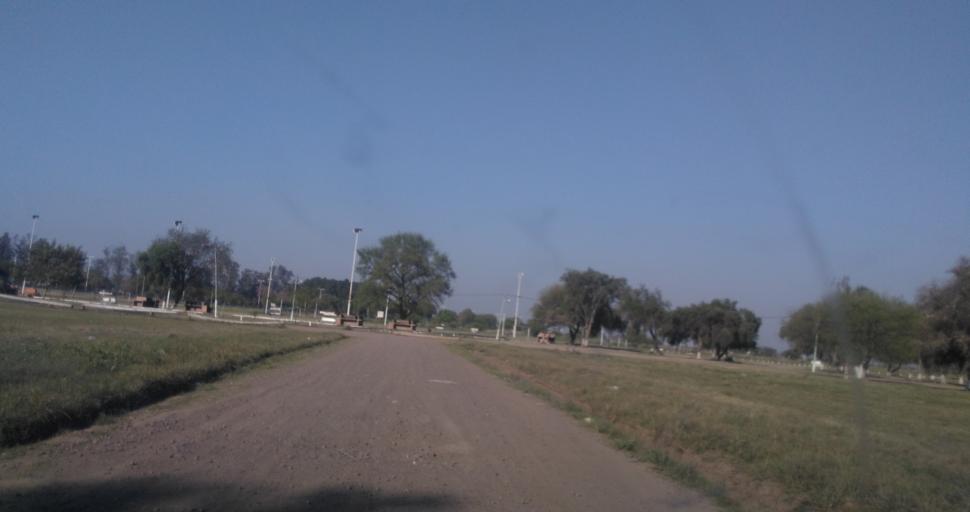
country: AR
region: Chaco
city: Fontana
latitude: -27.4386
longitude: -59.0324
